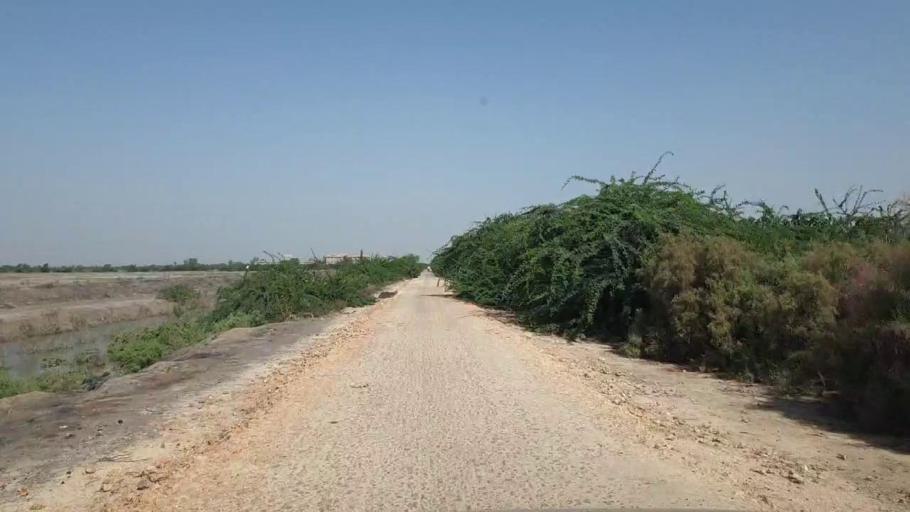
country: PK
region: Sindh
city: Tando Bago
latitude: 24.7337
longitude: 69.0744
